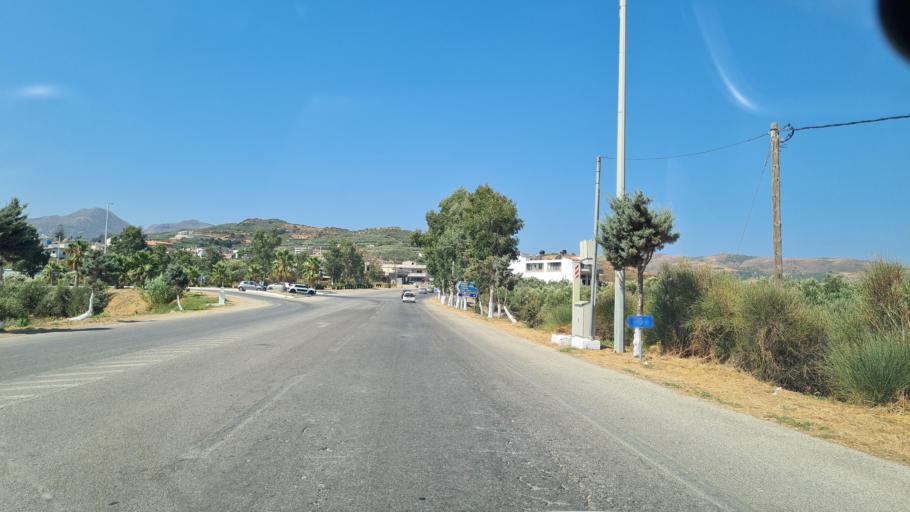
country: GR
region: Crete
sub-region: Nomos Chanias
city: Kissamos
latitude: 35.4931
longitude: 23.6698
